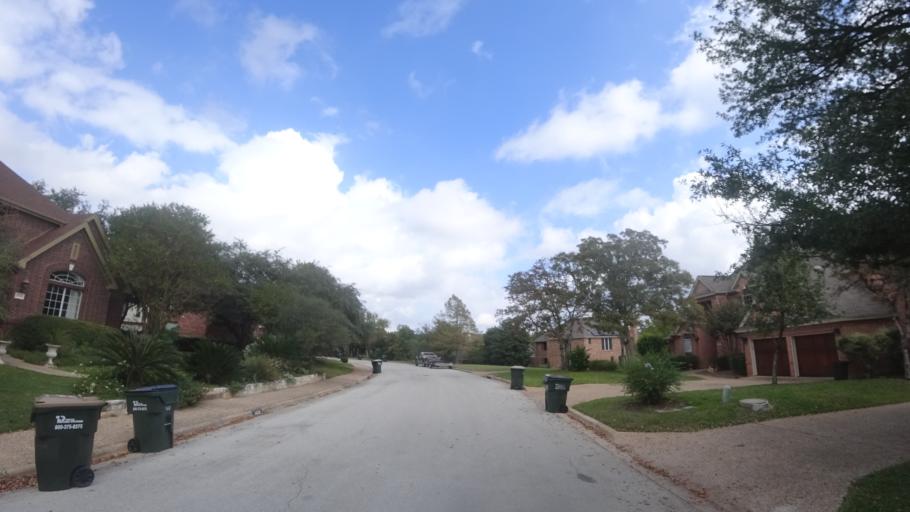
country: US
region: Texas
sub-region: Travis County
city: Barton Creek
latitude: 30.2953
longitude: -97.8954
